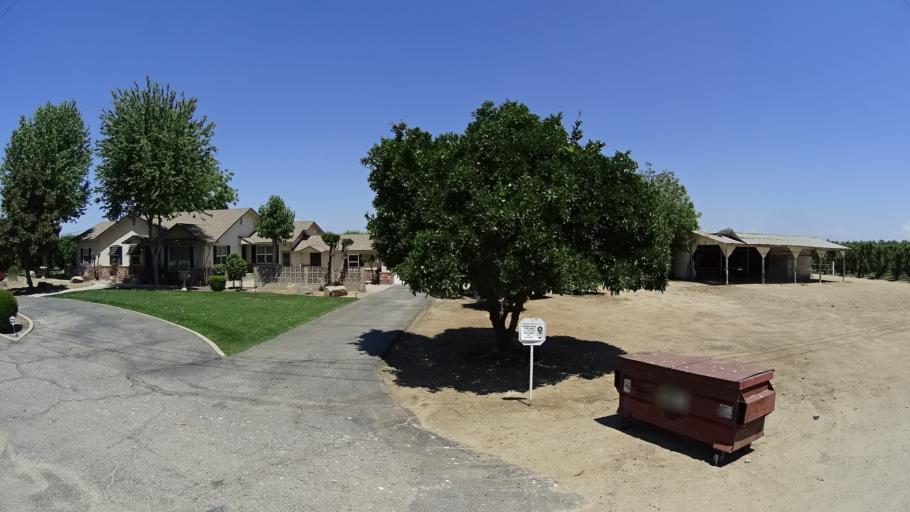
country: US
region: California
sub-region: Fresno County
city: Kingsburg
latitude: 36.4814
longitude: -119.5711
